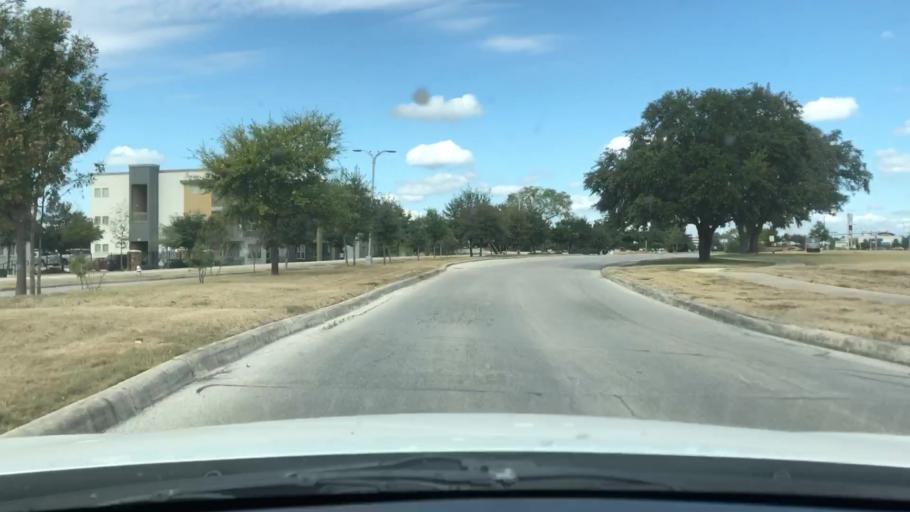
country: US
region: Texas
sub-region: Bexar County
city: San Antonio
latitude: 29.3488
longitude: -98.4478
